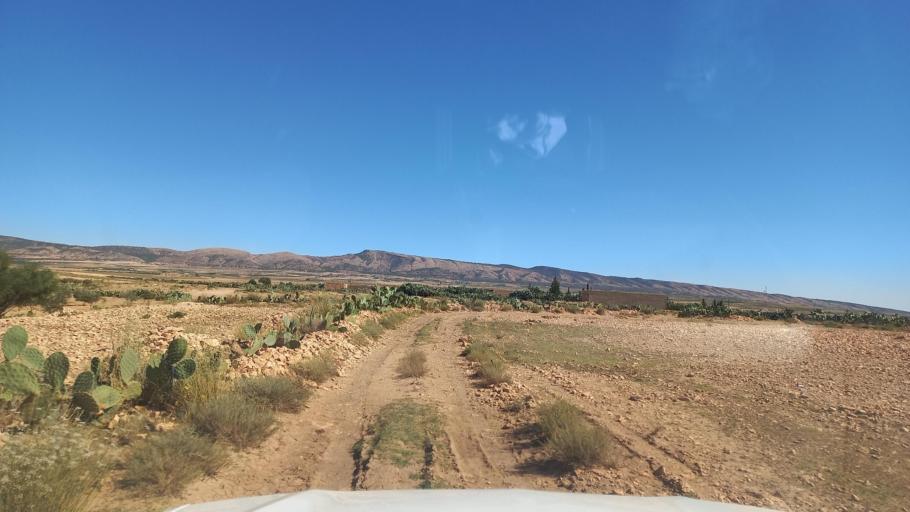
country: TN
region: Al Qasrayn
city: Sbiba
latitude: 35.3851
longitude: 9.0932
